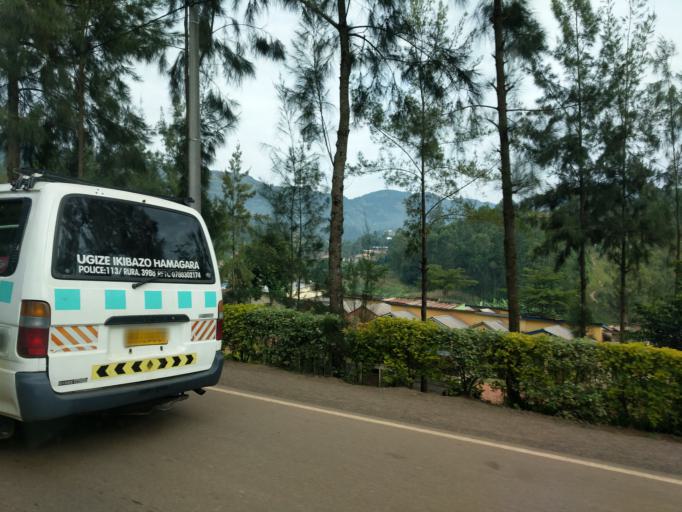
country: RW
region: Northern Province
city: Musanze
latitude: -1.6469
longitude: 29.7894
